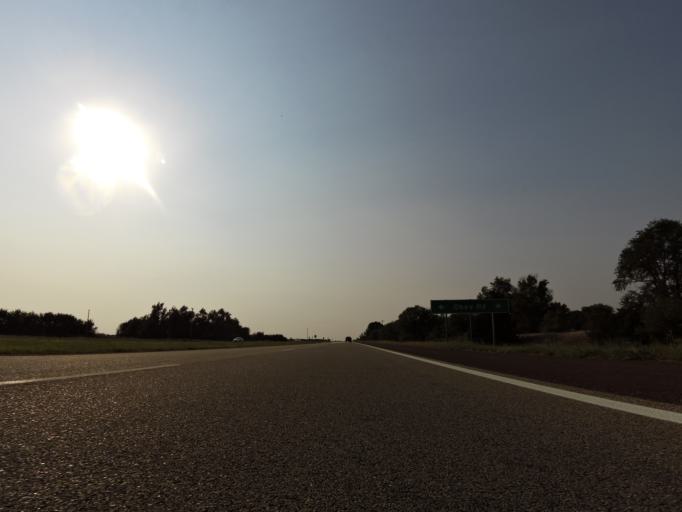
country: US
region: Kansas
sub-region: Reno County
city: Haven
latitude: 37.9284
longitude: -97.8465
